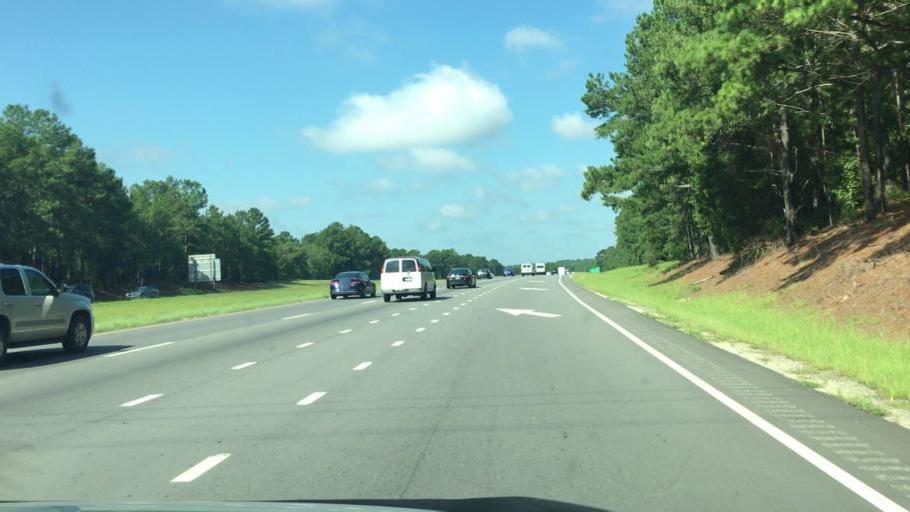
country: US
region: North Carolina
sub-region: Cumberland County
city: Hope Mills
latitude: 34.9729
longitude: -78.8655
